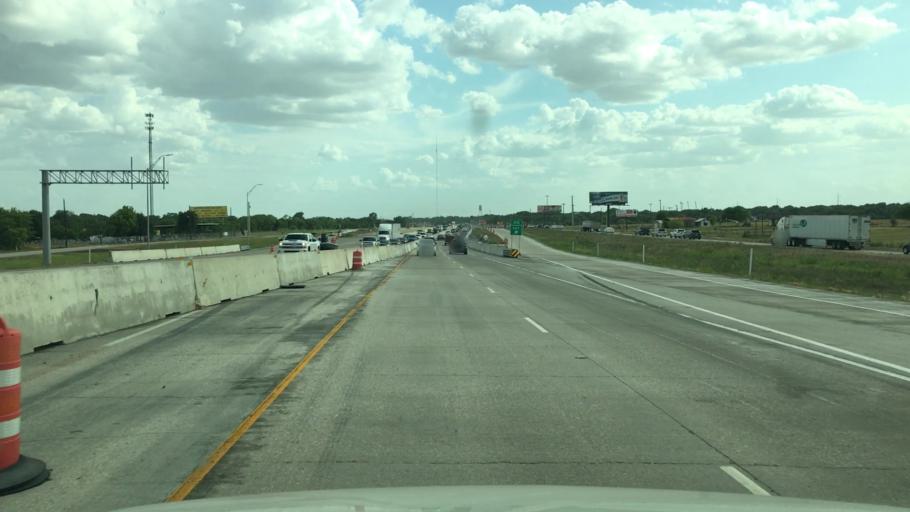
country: US
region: Texas
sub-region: McLennan County
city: Bruceville-Eddy
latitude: 31.3052
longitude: -97.2461
